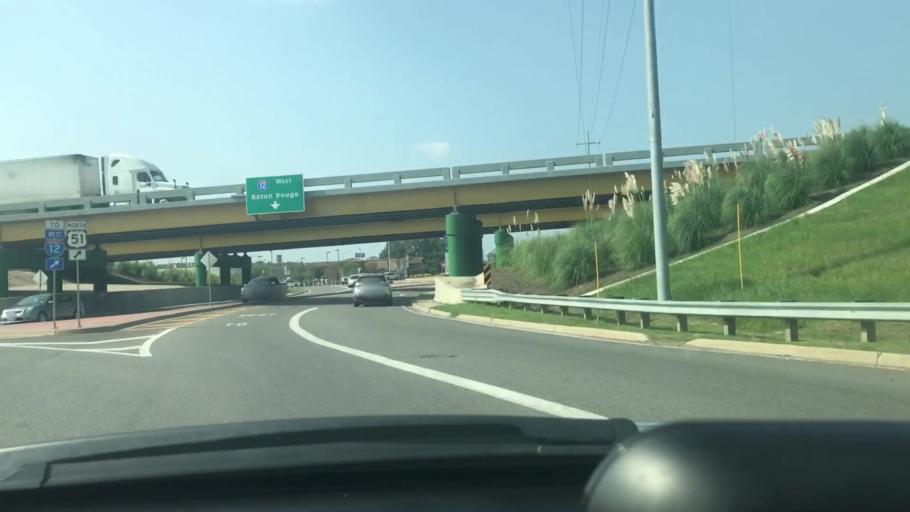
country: US
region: Louisiana
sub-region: Tangipahoa Parish
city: Hammond
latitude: 30.4784
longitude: -90.4570
